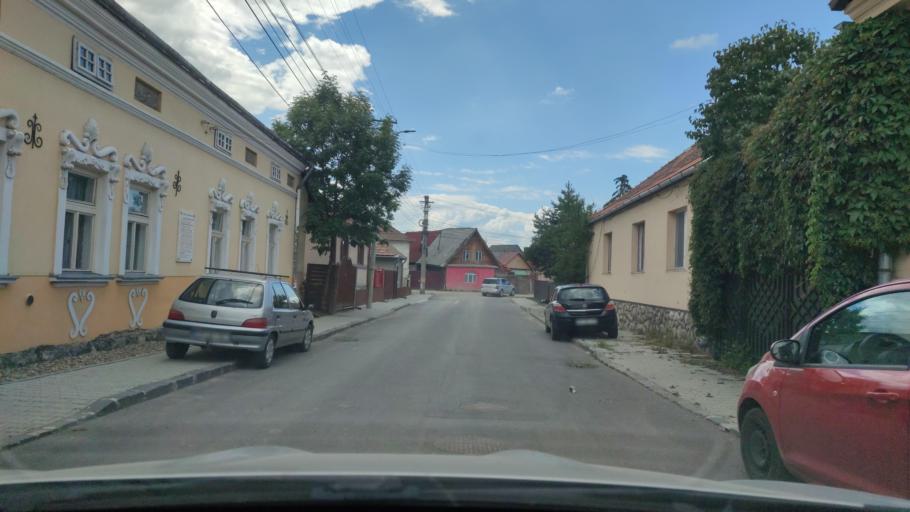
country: RO
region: Harghita
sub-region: Municipiul Gheorgheni
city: Gheorgheni
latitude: 46.7212
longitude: 25.6055
